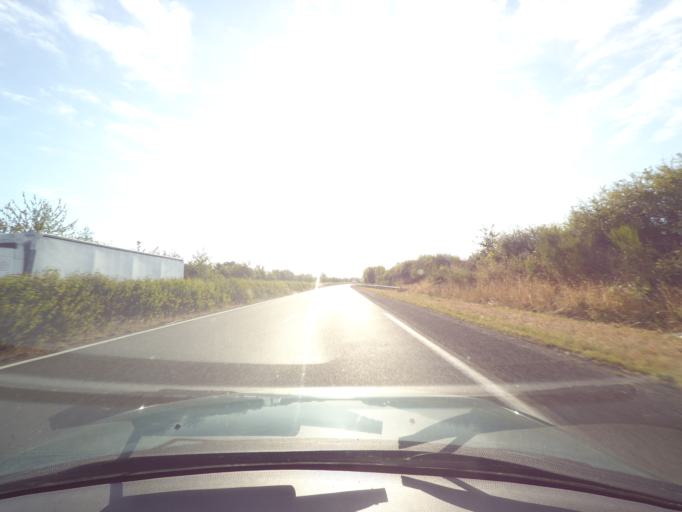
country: FR
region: Poitou-Charentes
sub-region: Departement des Deux-Sevres
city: Bressuire
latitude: 46.8363
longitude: -0.4502
